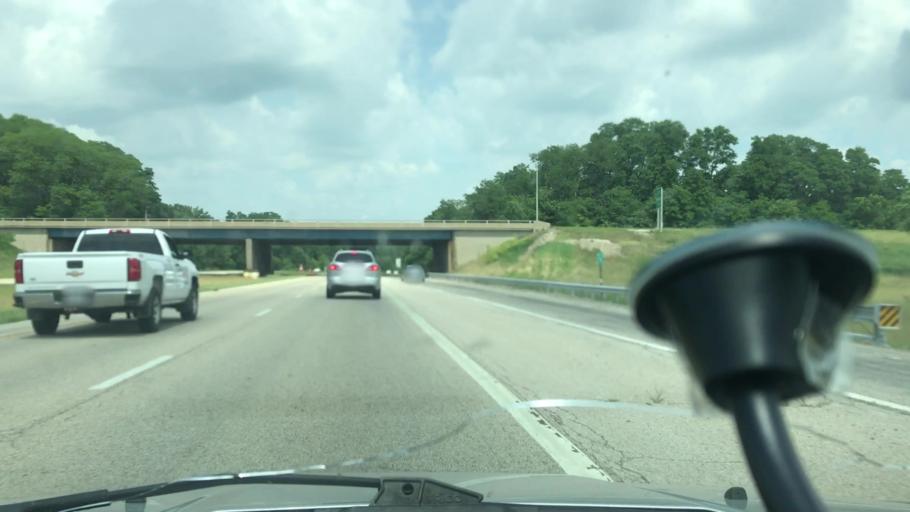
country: US
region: Illinois
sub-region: Peoria County
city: Bellevue
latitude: 40.6724
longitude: -89.6682
